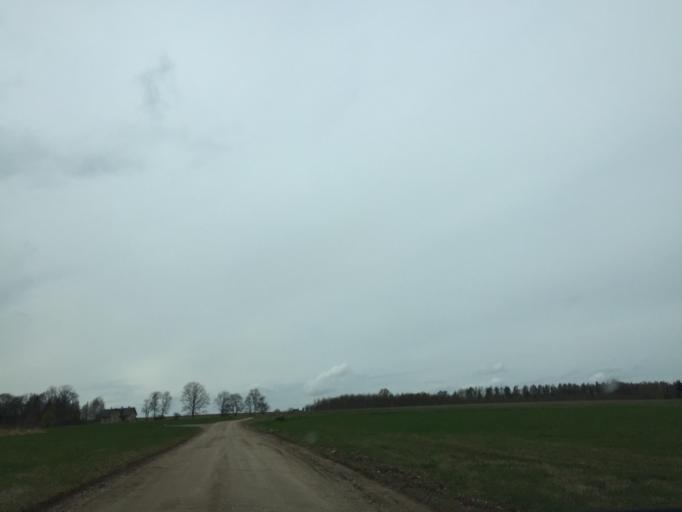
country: LV
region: Priekuli
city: Priekuli
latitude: 57.3331
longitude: 25.3829
